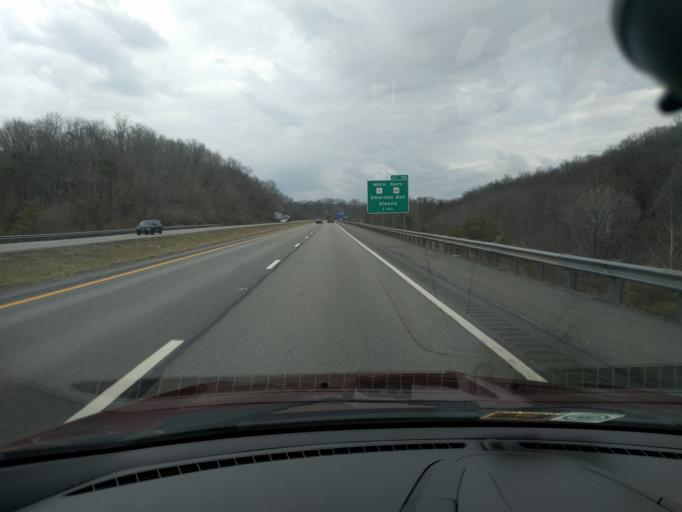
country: US
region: West Virginia
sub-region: Wood County
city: Vienna
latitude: 39.2985
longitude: -81.4913
